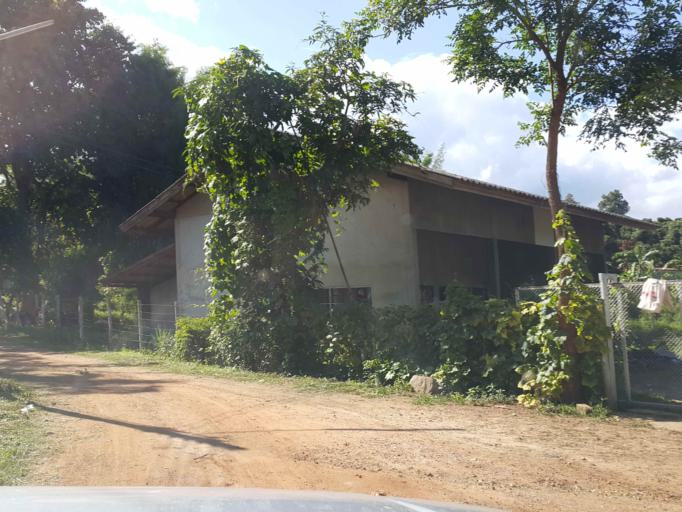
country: TH
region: Chiang Mai
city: Mae Taeng
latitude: 18.9729
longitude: 98.8931
